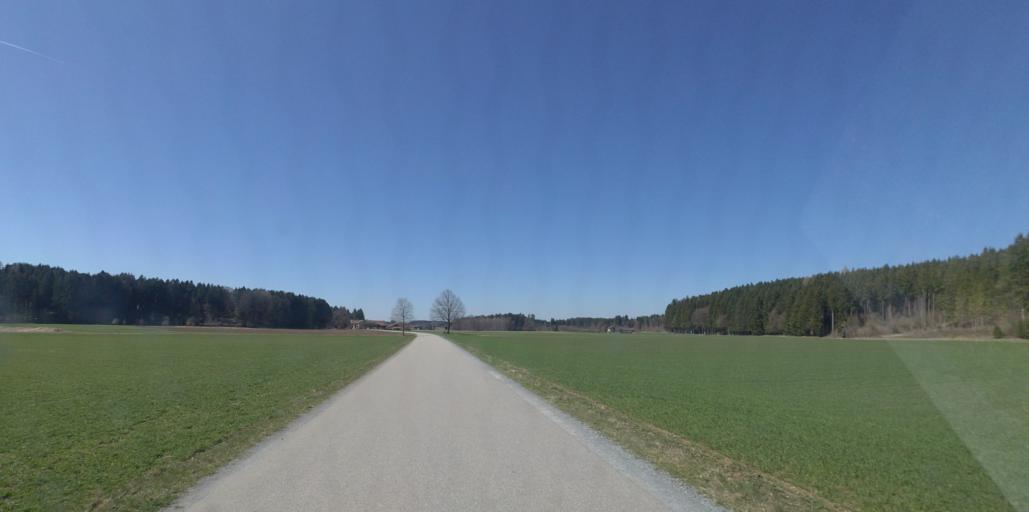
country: DE
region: Bavaria
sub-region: Upper Bavaria
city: Chieming
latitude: 47.9124
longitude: 12.5529
